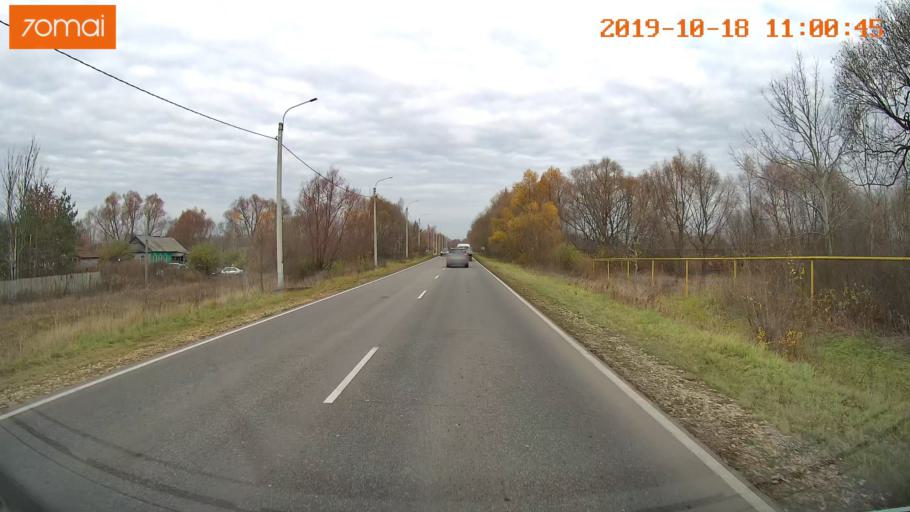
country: RU
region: Tula
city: Yepifan'
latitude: 53.8468
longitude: 38.5527
